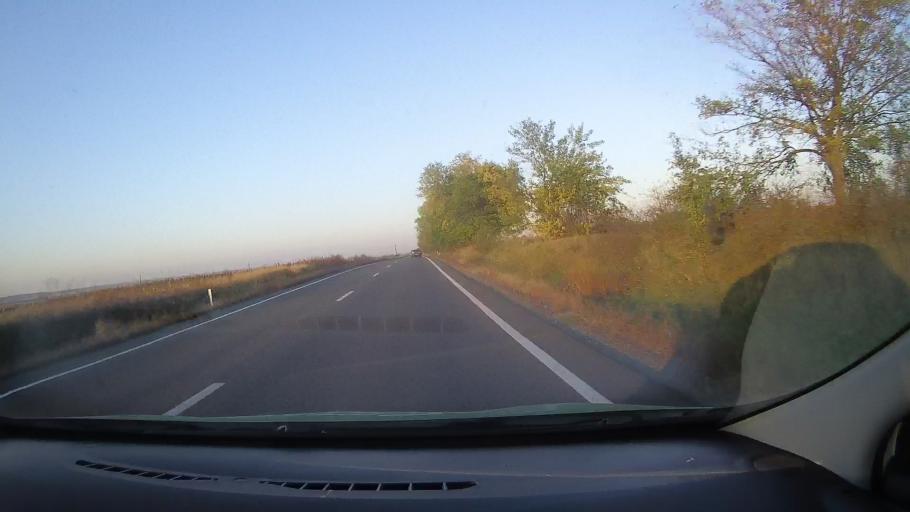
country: RO
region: Bihor
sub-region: Comuna Rosiori
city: Rosiori
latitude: 47.2694
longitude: 21.9745
